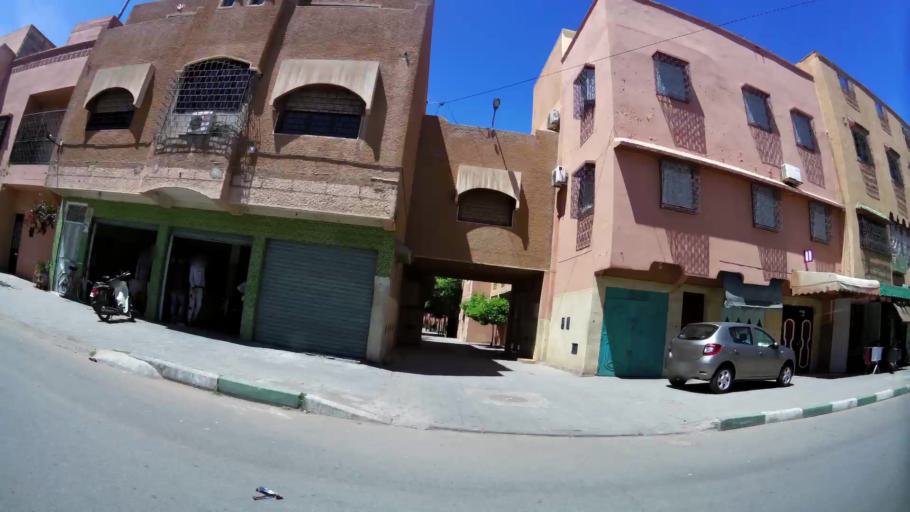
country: MA
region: Marrakech-Tensift-Al Haouz
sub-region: Marrakech
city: Marrakesh
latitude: 31.6320
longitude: -8.0502
